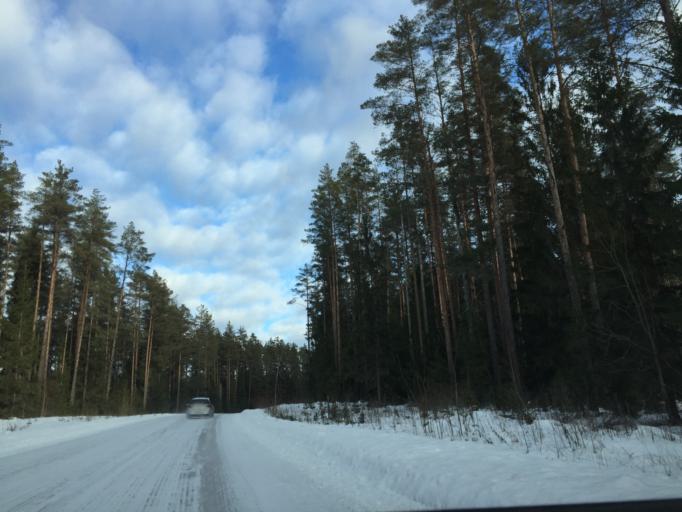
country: LV
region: Ogre
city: Jumprava
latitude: 56.5583
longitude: 24.9029
